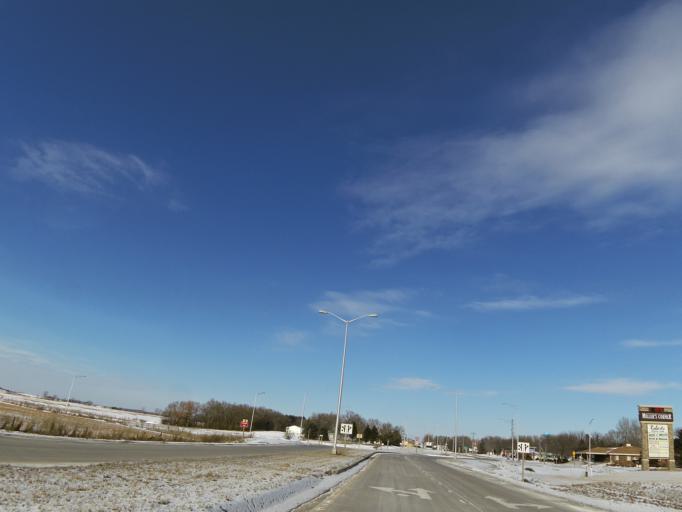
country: US
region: Wisconsin
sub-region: Saint Croix County
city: Roberts
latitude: 44.9768
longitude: -92.5581
